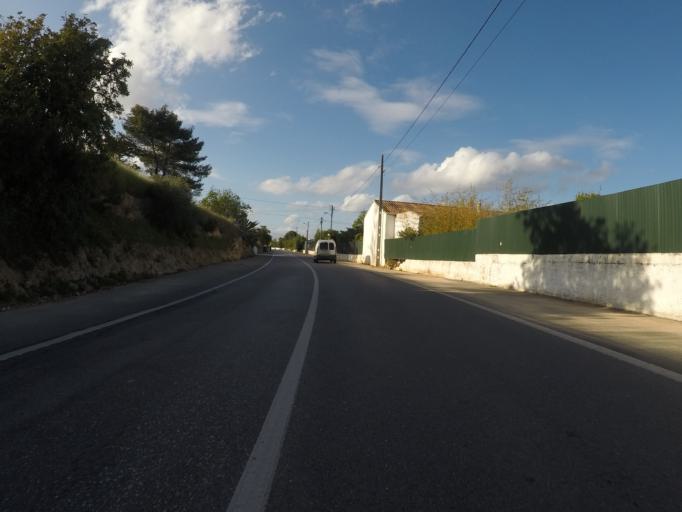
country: PT
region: Faro
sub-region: Lagoa
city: Lagoa
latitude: 37.1134
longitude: -8.4550
